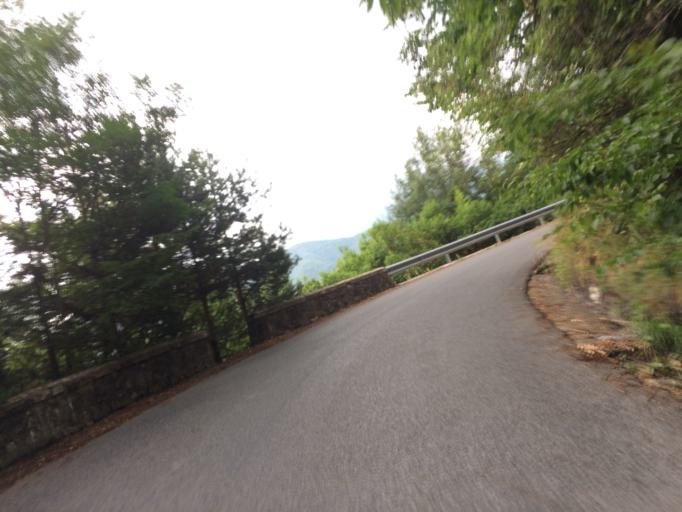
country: IT
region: Liguria
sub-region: Provincia di Imperia
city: Triora
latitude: 43.9835
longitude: 7.7603
